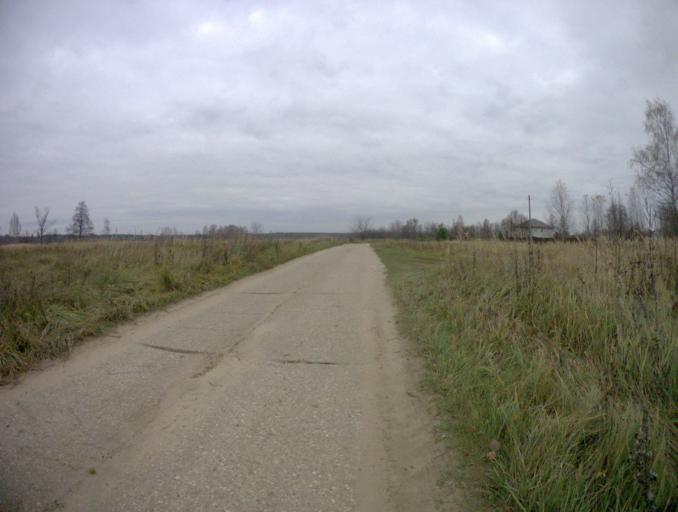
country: RU
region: Moskovskaya
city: Malaya Dubna
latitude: 55.9903
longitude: 38.9668
